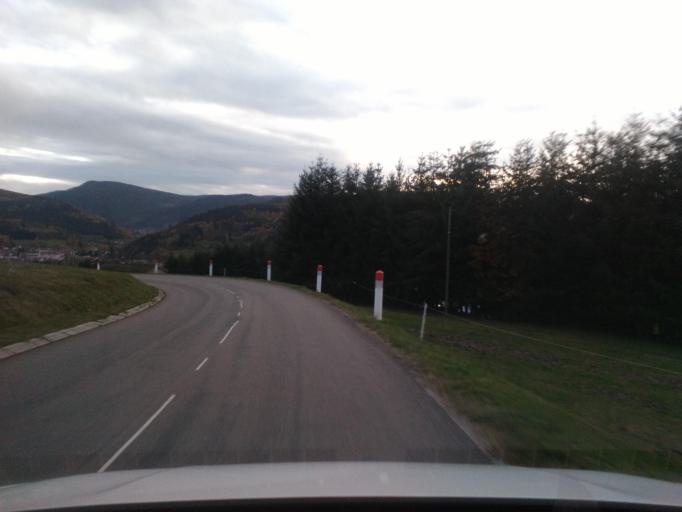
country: FR
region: Lorraine
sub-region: Departement des Vosges
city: Fraize
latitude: 48.1903
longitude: 7.0134
